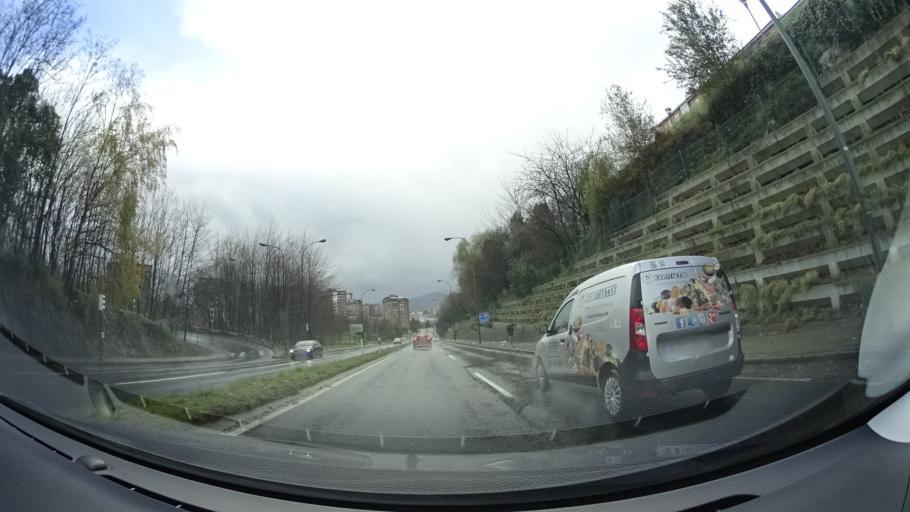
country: ES
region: Basque Country
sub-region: Bizkaia
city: Santutxu
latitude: 43.2550
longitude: -2.9101
